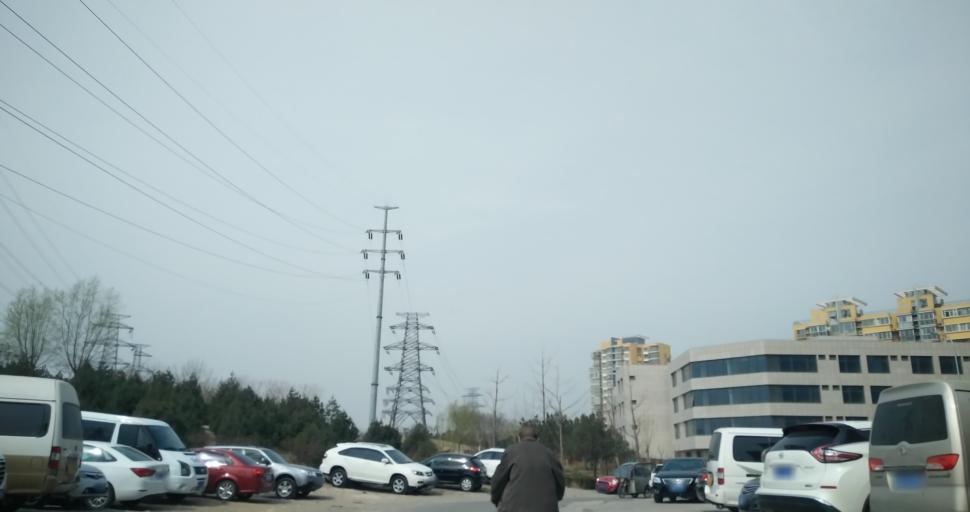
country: CN
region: Beijing
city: Jiugong
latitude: 39.8535
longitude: 116.4964
